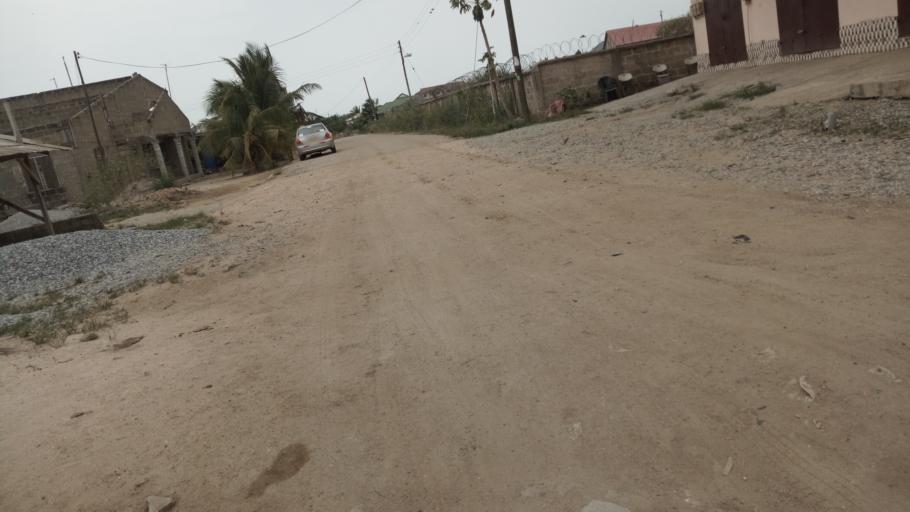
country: GH
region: Central
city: Winneba
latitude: 5.3827
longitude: -0.6393
